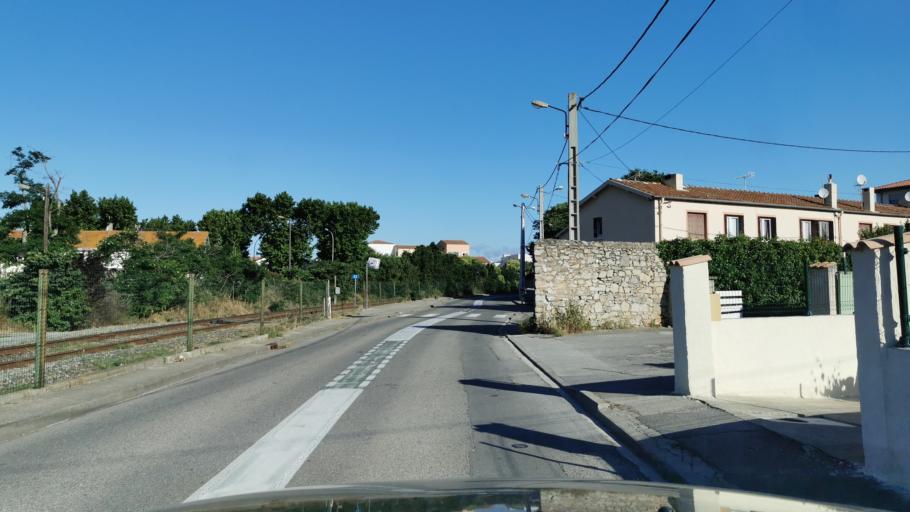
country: FR
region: Languedoc-Roussillon
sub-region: Departement de l'Aude
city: Narbonne
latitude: 43.1831
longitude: 2.9905
